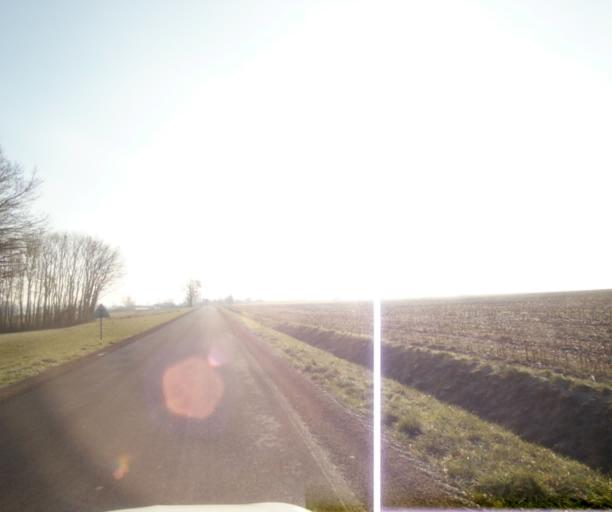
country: FR
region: Champagne-Ardenne
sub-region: Departement de la Haute-Marne
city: Montier-en-Der
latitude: 48.4854
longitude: 4.7434
